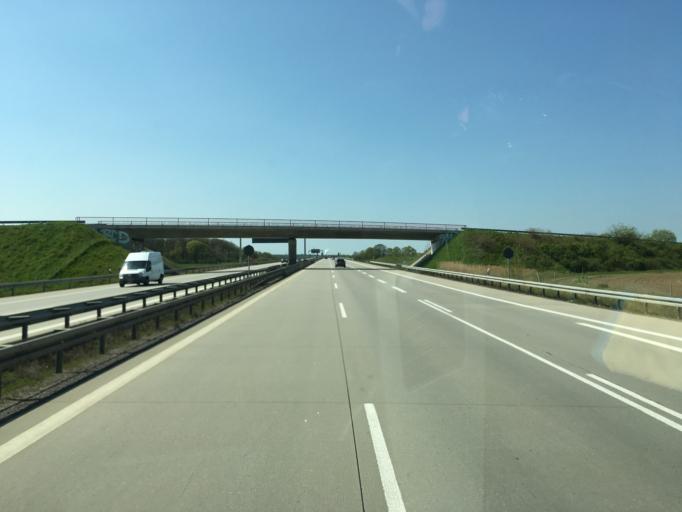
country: DE
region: Saxony
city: Borsdorf
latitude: 51.3036
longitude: 12.5460
